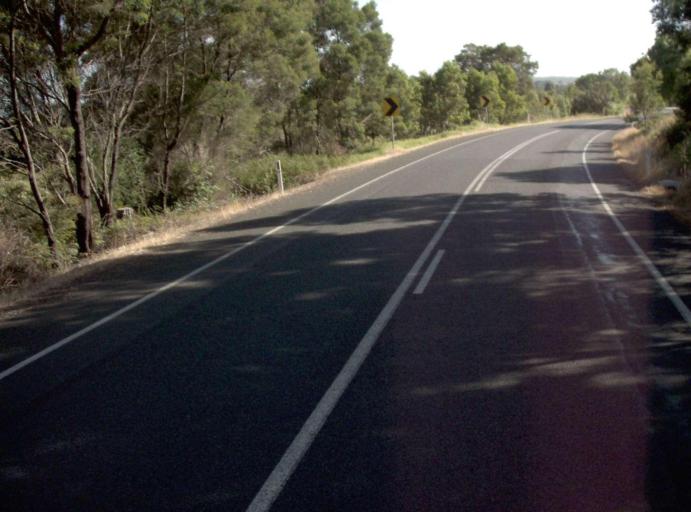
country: AU
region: Victoria
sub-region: East Gippsland
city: Lakes Entrance
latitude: -37.8492
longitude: 147.8485
